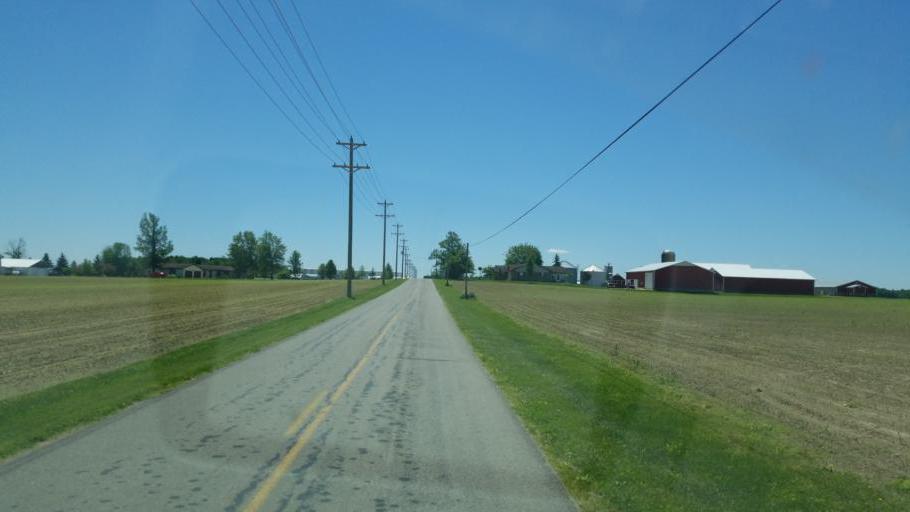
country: US
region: Ohio
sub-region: Mercer County
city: Fort Recovery
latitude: 40.3739
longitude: -84.7290
